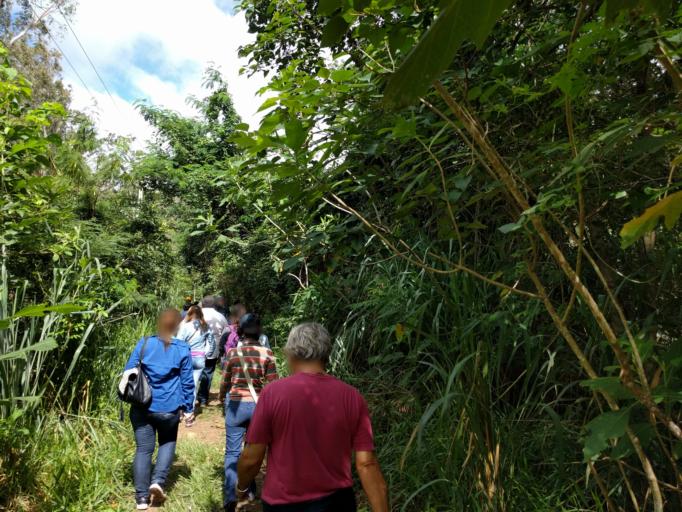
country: BO
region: Santa Cruz
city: Santa Cruz de la Sierra
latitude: -17.7955
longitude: -63.2253
